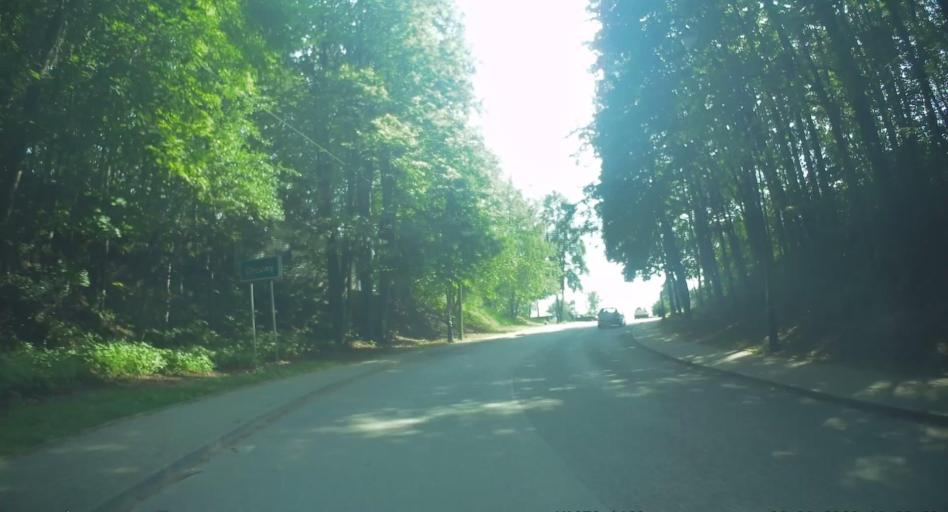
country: PL
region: Swietokrzyskie
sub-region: Powiat kielecki
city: Checiny
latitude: 50.7975
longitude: 20.4564
